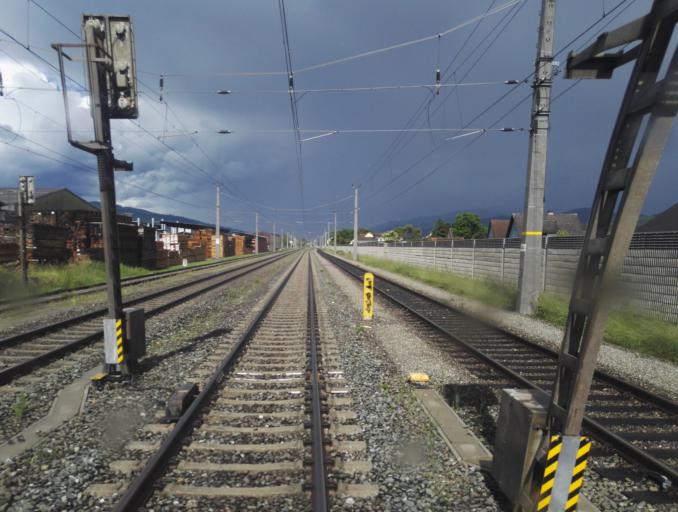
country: AT
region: Styria
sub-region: Politischer Bezirk Bruck-Muerzzuschlag
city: Sankt Marein im Muerztal
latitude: 47.4706
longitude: 15.3673
